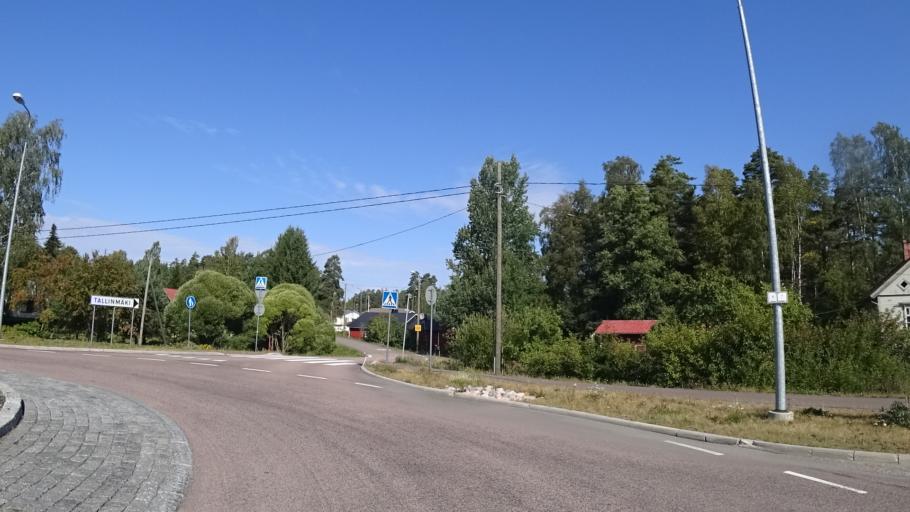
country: FI
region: Kymenlaakso
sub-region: Kotka-Hamina
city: Hamina
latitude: 60.5555
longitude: 27.2370
